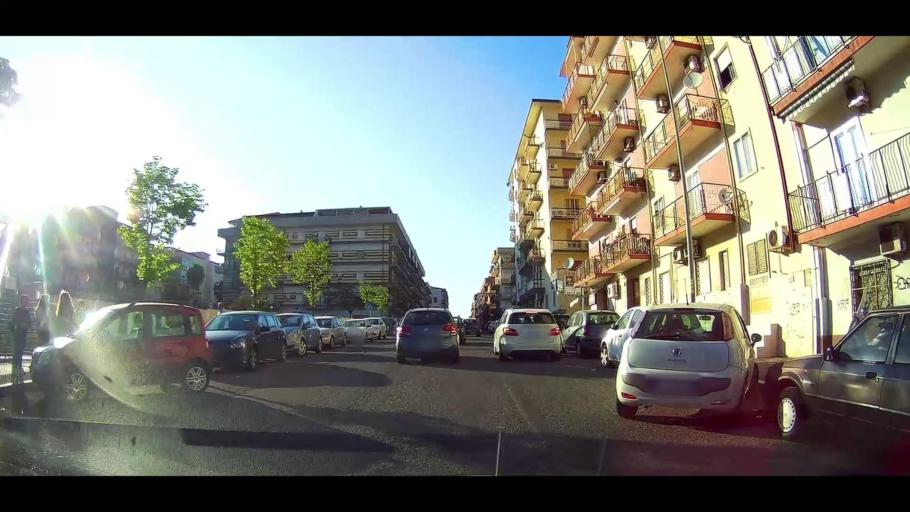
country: IT
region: Calabria
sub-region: Provincia di Crotone
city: Crotone
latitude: 39.0758
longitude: 17.1287
